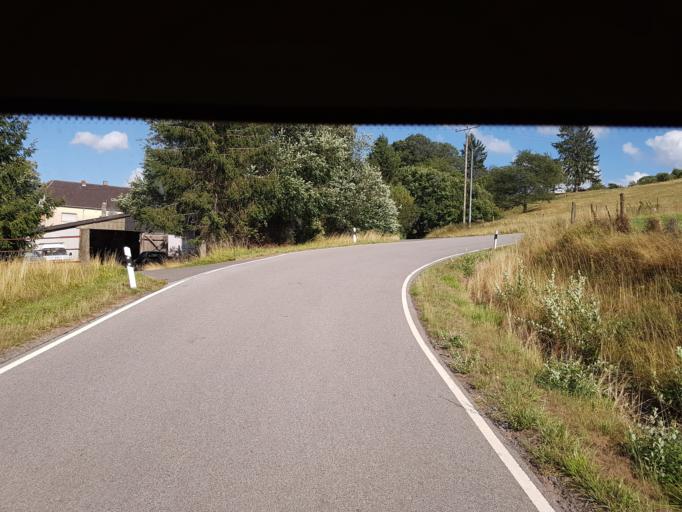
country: DE
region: Rheinland-Pfalz
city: Fisch
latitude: 49.6120
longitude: 6.4966
